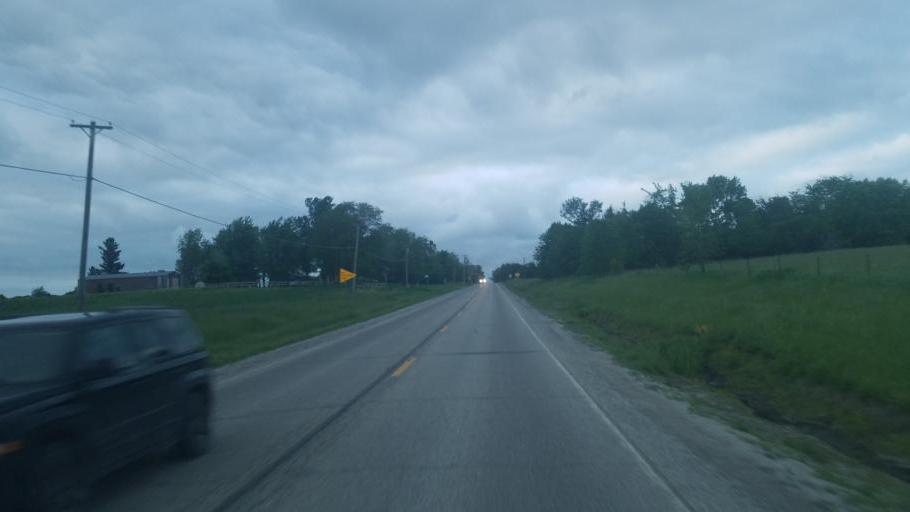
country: US
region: Iowa
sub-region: Decatur County
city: Lamoni
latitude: 40.6101
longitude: -93.9389
